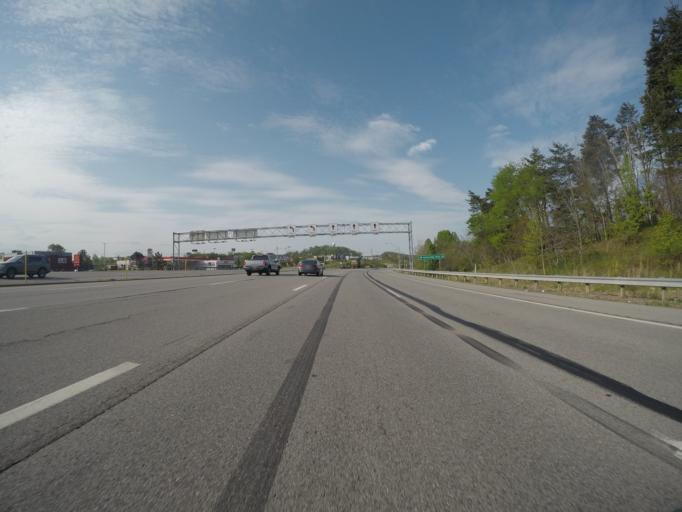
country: US
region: West Virginia
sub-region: Kanawha County
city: Dunbar
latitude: 38.3216
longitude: -81.7168
